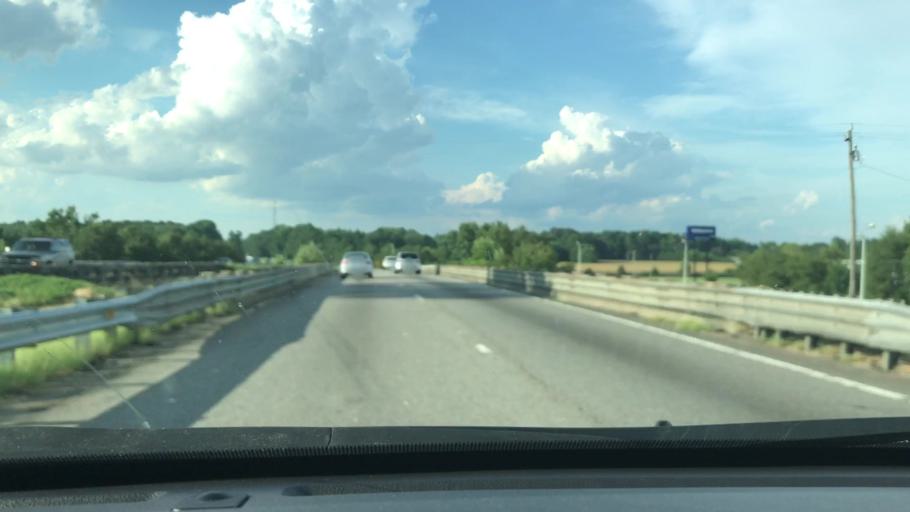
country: US
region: North Carolina
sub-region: Robeson County
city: Saint Pauls
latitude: 34.8108
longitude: -78.9862
